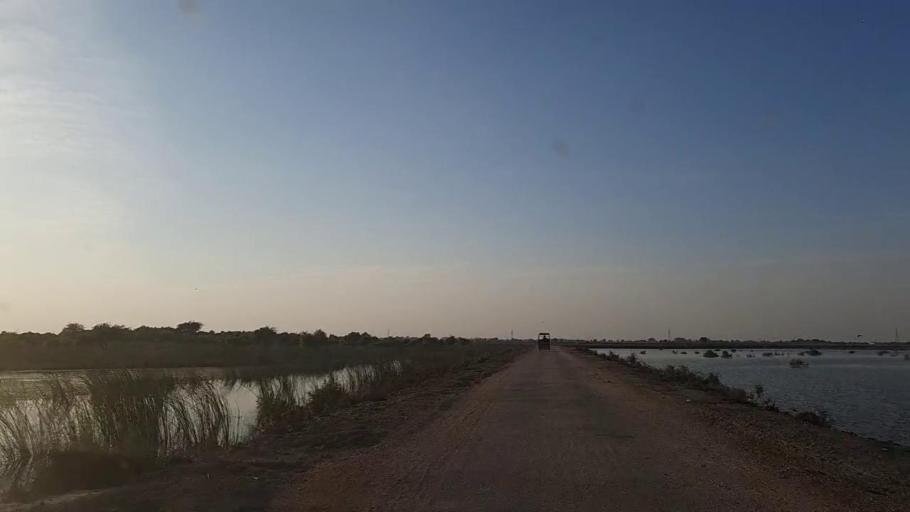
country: PK
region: Sindh
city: Mirpur Batoro
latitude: 24.6858
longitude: 68.2058
